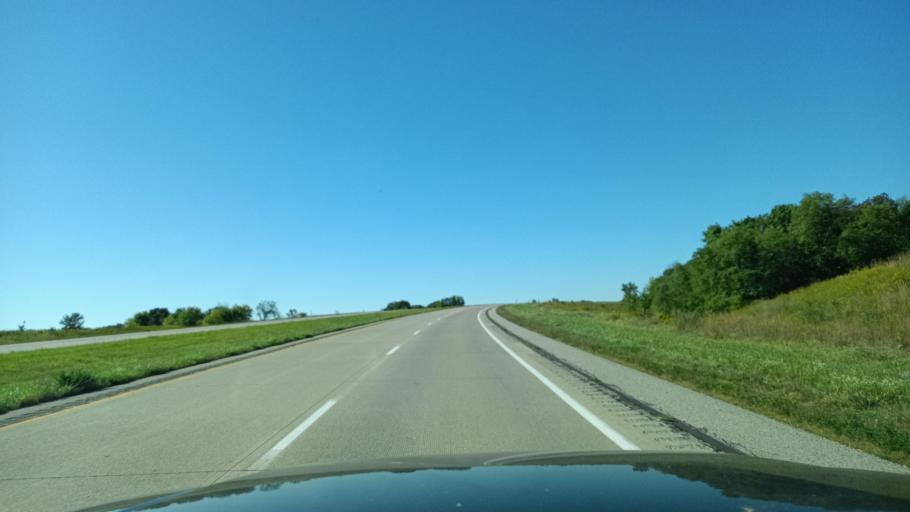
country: US
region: Iowa
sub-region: Lee County
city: Fort Madison
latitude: 40.6551
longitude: -91.3618
